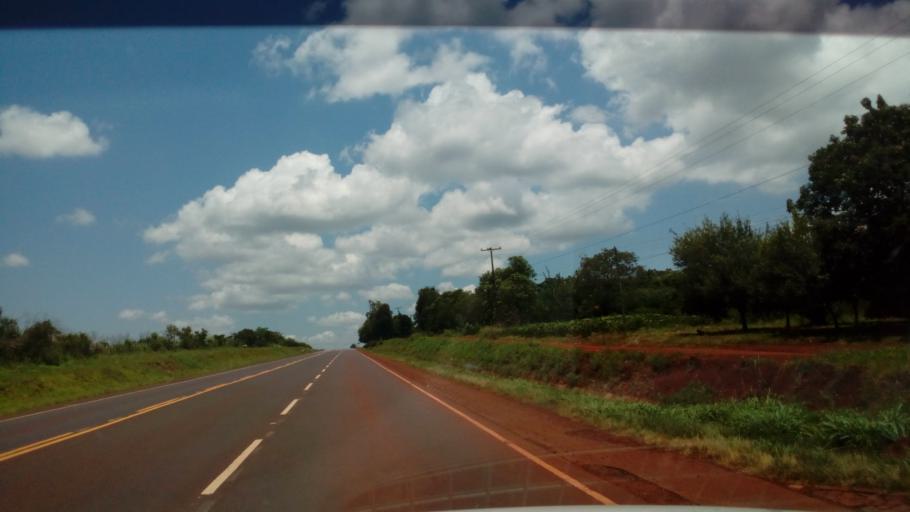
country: PY
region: Itapua
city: Arquitecto Tomas Romero Pereira
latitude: -26.4245
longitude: -55.2343
